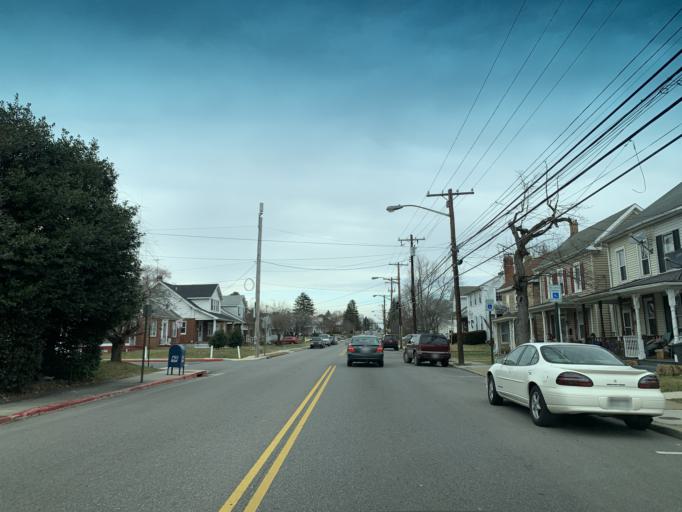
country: US
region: Maryland
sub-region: Washington County
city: Hagerstown
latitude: 39.6539
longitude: -77.7311
